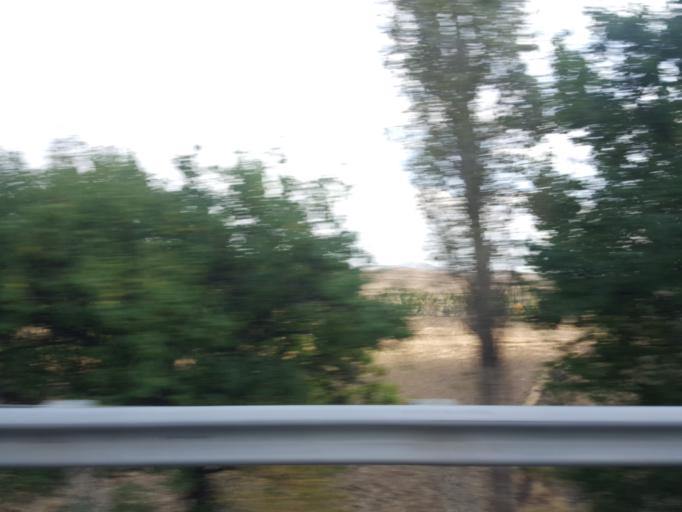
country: TR
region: Corum
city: Sungurlu
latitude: 40.2130
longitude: 34.5508
